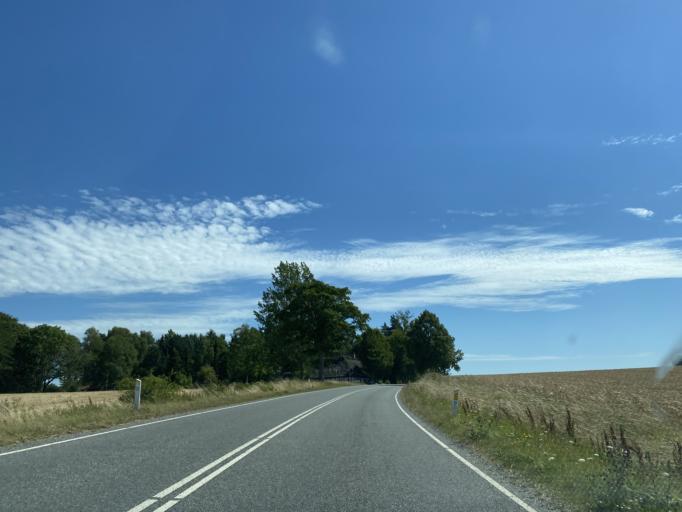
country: DK
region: South Denmark
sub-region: Faaborg-Midtfyn Kommune
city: Ringe
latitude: 55.2446
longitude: 10.5515
